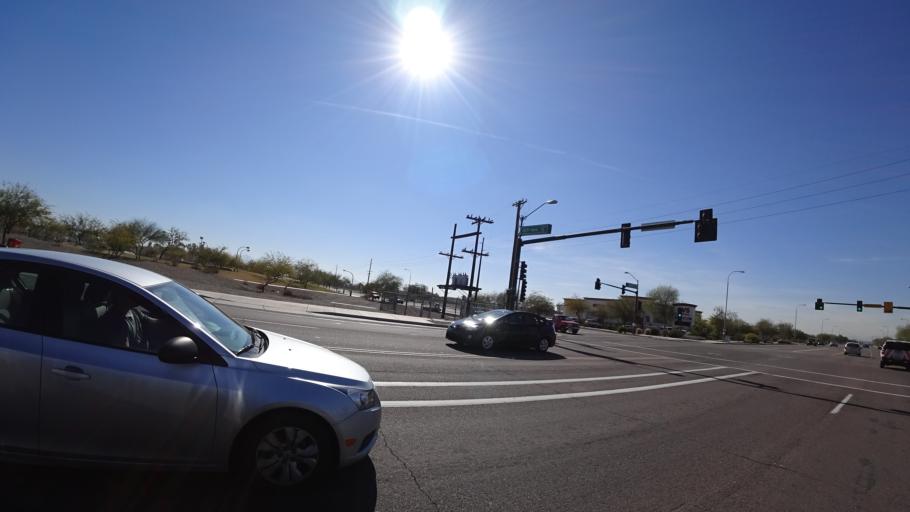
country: US
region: Arizona
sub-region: Maricopa County
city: Tolleson
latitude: 33.5083
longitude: -112.2895
